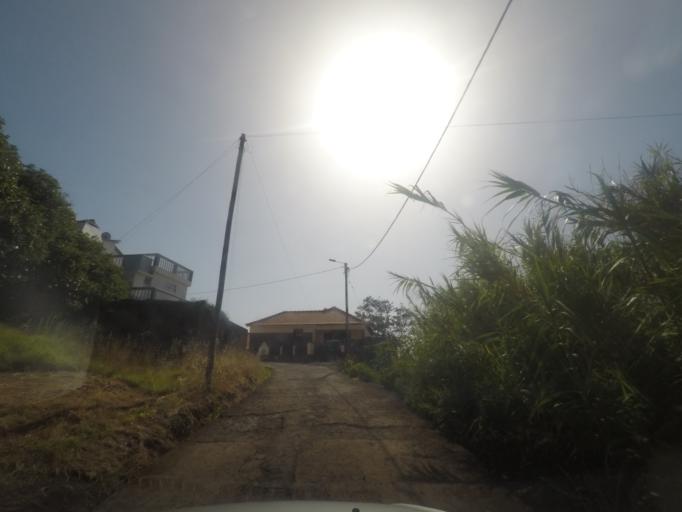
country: PT
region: Madeira
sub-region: Calheta
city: Faja da Ovelha
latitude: 32.8105
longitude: -17.2487
